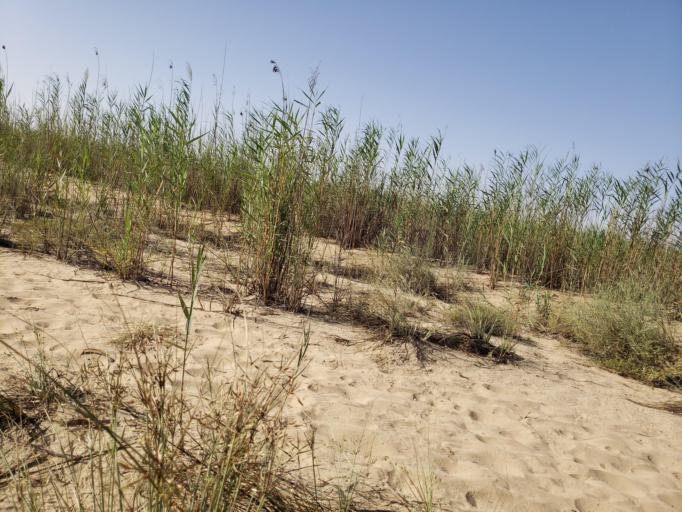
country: AE
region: Dubai
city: Dubai
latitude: 24.9712
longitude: 55.2105
